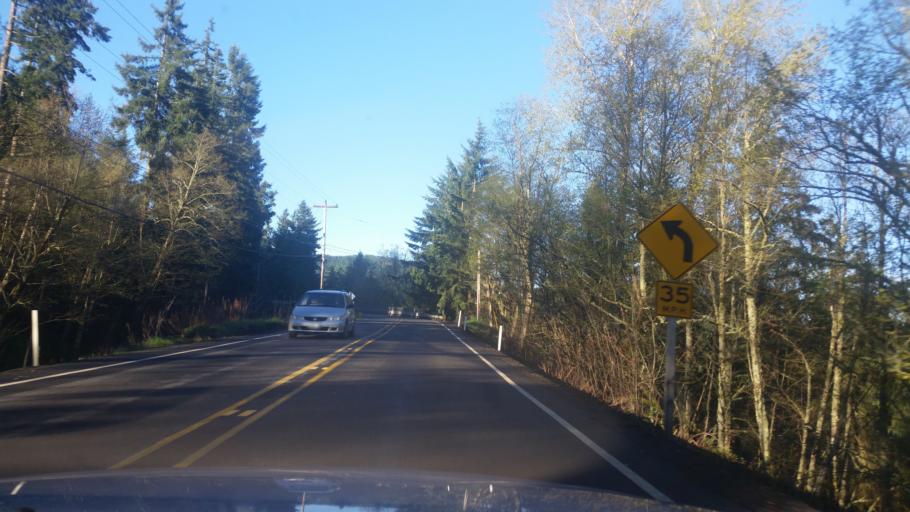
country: US
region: Washington
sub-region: Pierce County
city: Eatonville
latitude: 46.8504
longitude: -122.2705
